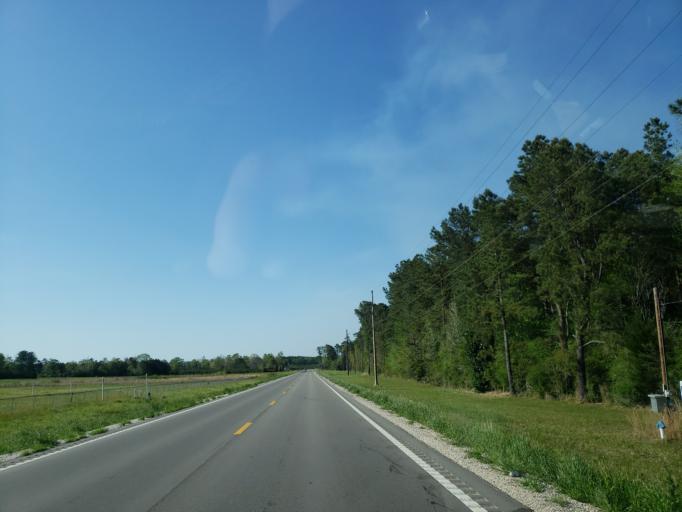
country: US
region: Mississippi
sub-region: Perry County
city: Richton
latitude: 31.3203
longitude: -88.9328
